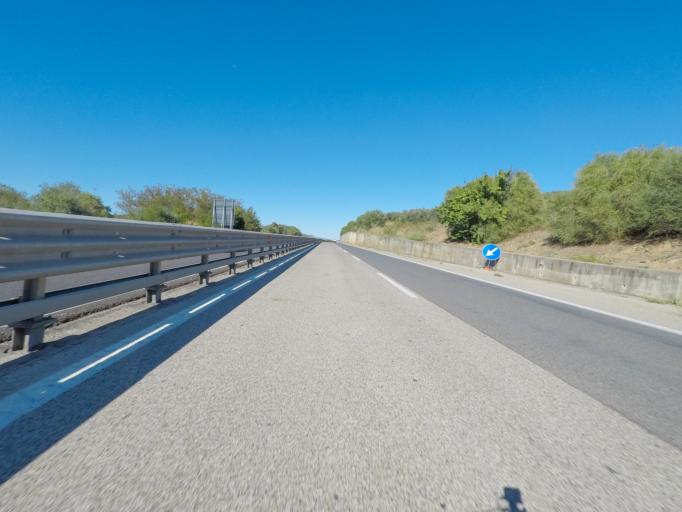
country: IT
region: Tuscany
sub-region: Provincia di Grosseto
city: Grosseto
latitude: 42.7352
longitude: 11.1368
